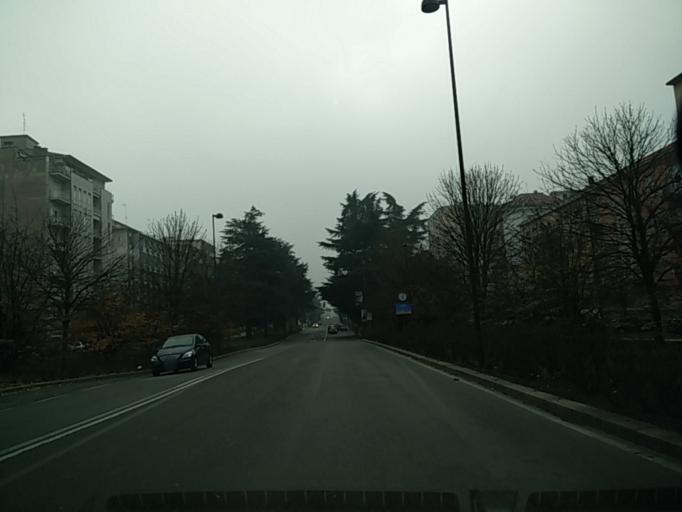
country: IT
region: Lombardy
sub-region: Provincia di Pavia
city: Pavia
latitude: 45.1859
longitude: 9.1468
